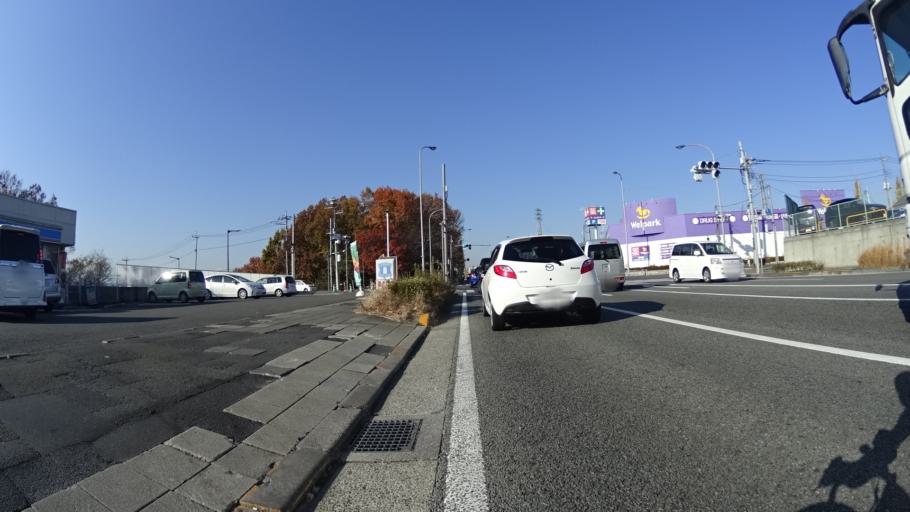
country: JP
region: Tokyo
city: Hino
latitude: 35.6688
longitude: 139.3930
